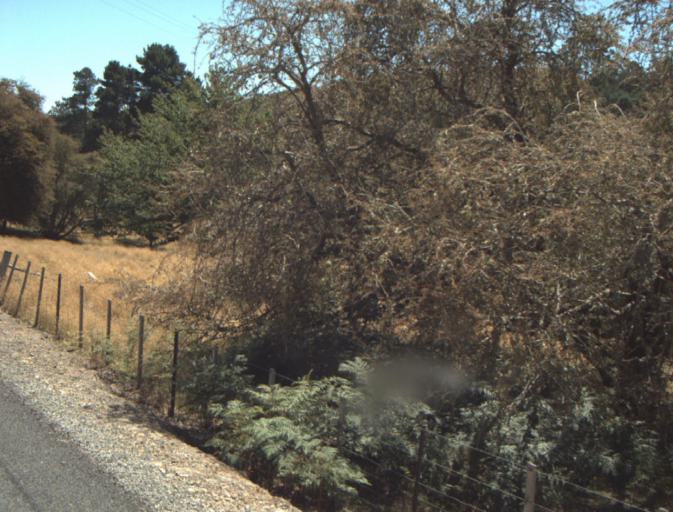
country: AU
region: Tasmania
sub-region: Dorset
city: Scottsdale
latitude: -41.2963
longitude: 147.3535
